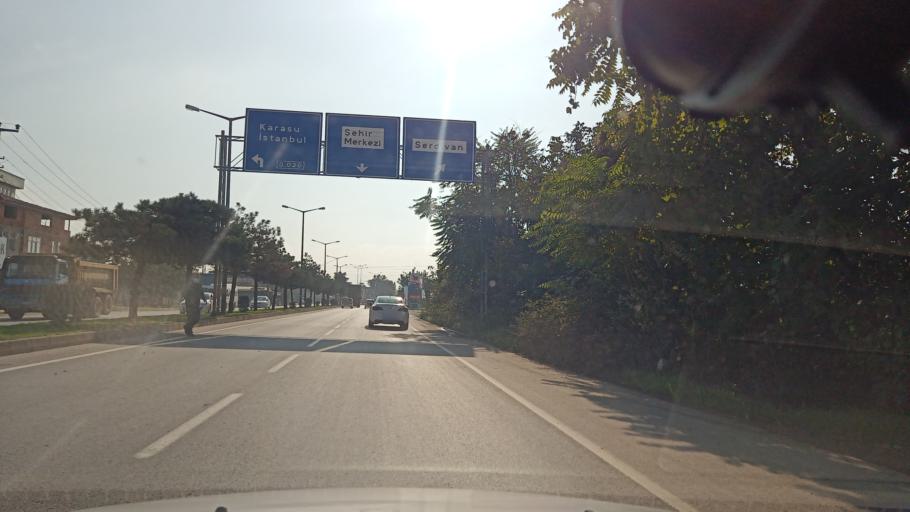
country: TR
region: Sakarya
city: Adapazari
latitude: 40.8028
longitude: 30.4061
